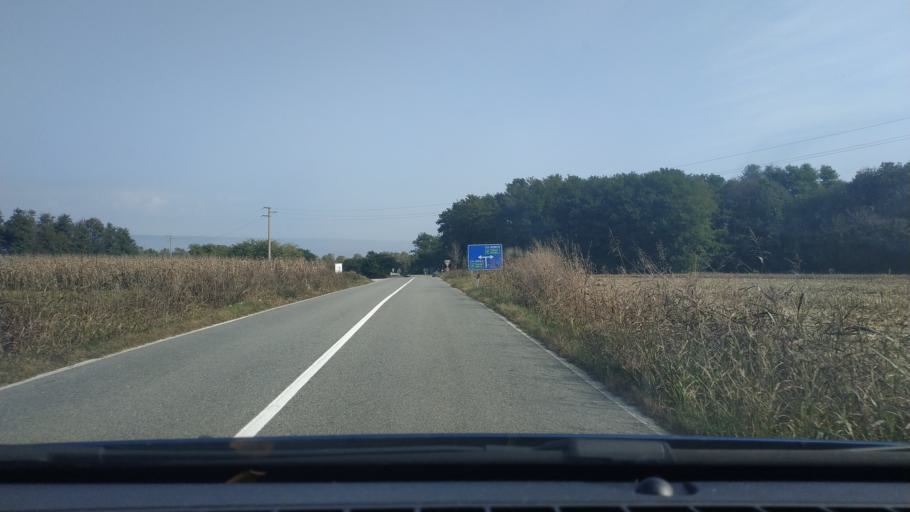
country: IT
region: Piedmont
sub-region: Provincia di Torino
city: Romano Canavese
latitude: 45.4097
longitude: 7.8792
